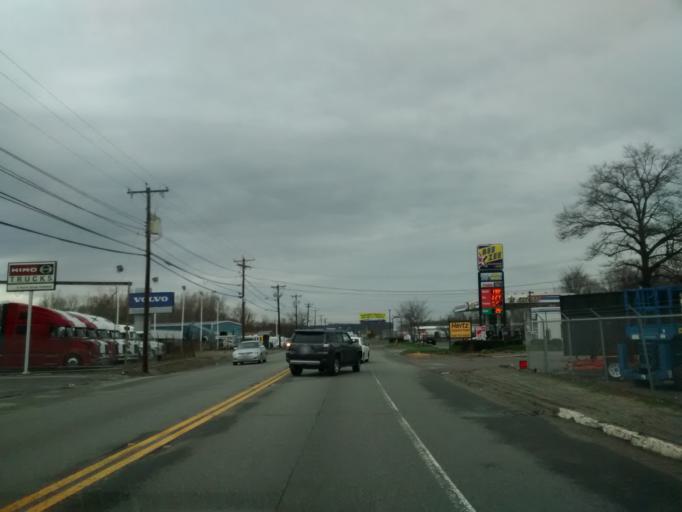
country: US
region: Massachusetts
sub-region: Worcester County
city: Sunderland
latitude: 42.2302
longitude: -71.7543
